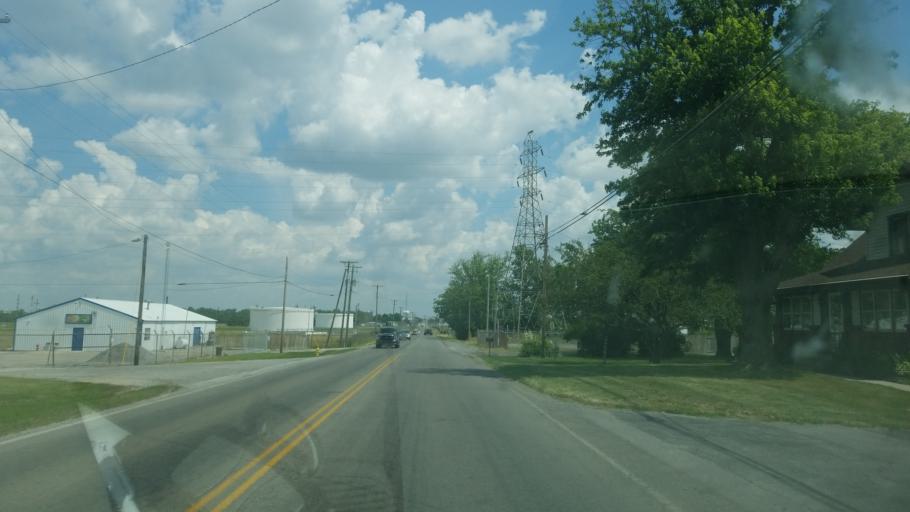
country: US
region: Ohio
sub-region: Allen County
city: Fort Shawnee
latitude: 40.7003
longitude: -84.1222
